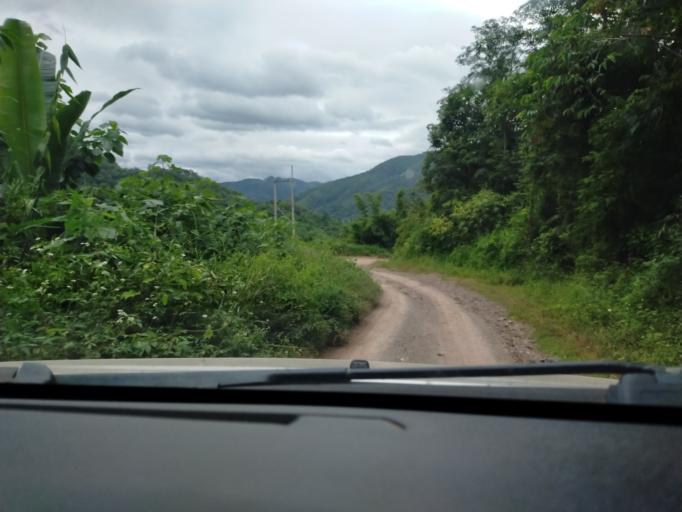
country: TH
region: Nan
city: Chaloem Phra Kiat
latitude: 19.8096
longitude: 101.3625
